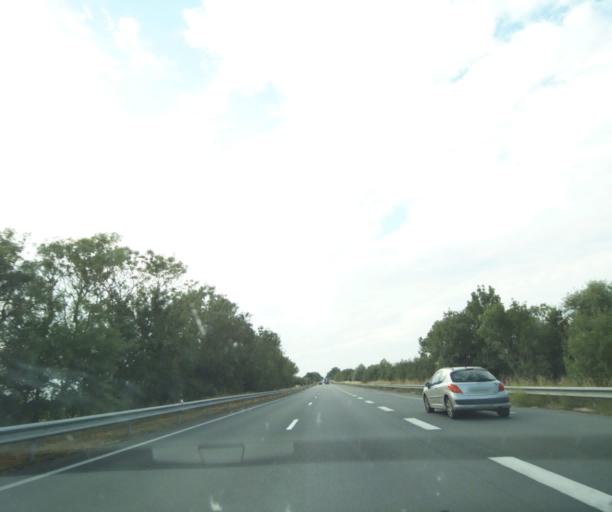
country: FR
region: Poitou-Charentes
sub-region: Departement de la Charente-Maritime
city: Chatelaillon-Plage
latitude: 46.0649
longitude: -1.0637
